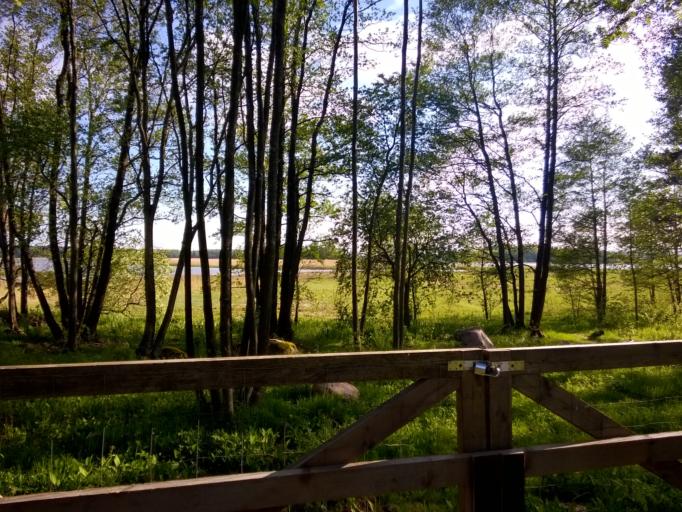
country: FI
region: Uusimaa
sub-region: Helsinki
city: Vantaa
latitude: 60.2145
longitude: 25.0141
